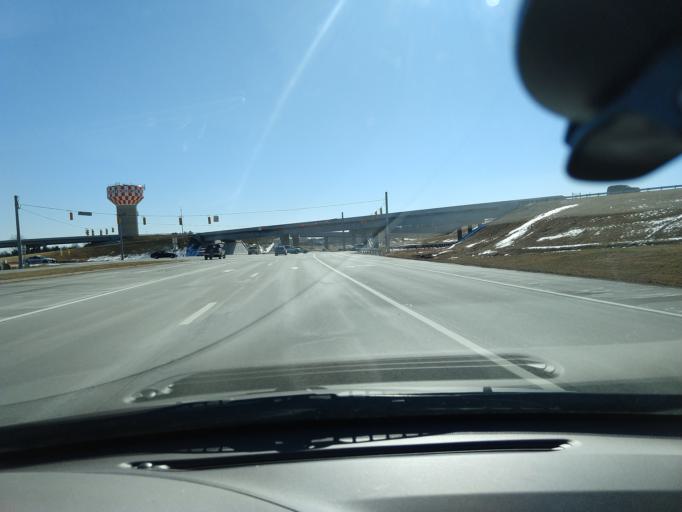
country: US
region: North Carolina
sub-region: Guilford County
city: Oak Ridge
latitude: 36.1255
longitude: -79.9620
